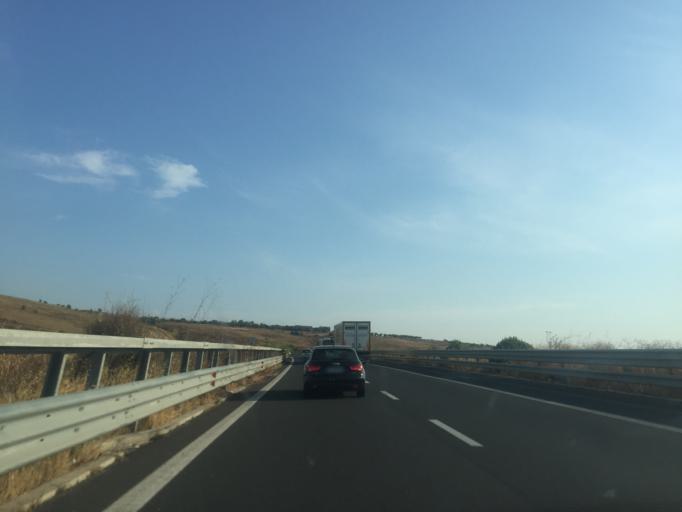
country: IT
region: Sicily
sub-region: Provincia di Siracusa
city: Lentini
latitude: 37.3560
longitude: 15.0474
